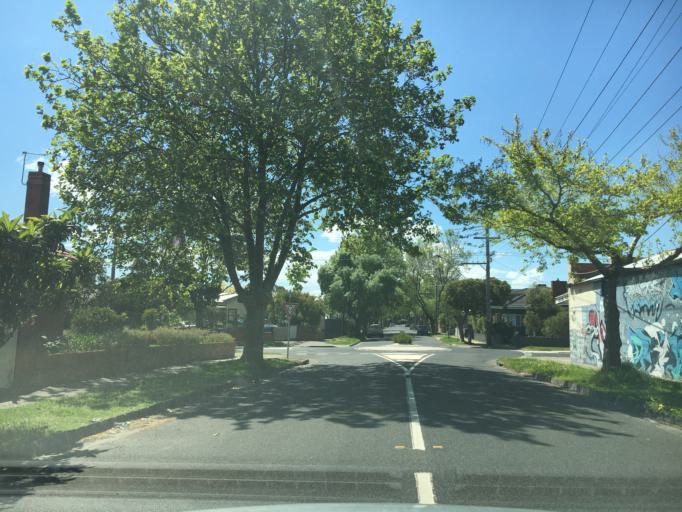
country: AU
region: Victoria
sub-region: Monash
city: Chadstone
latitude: -37.9035
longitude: 145.1010
